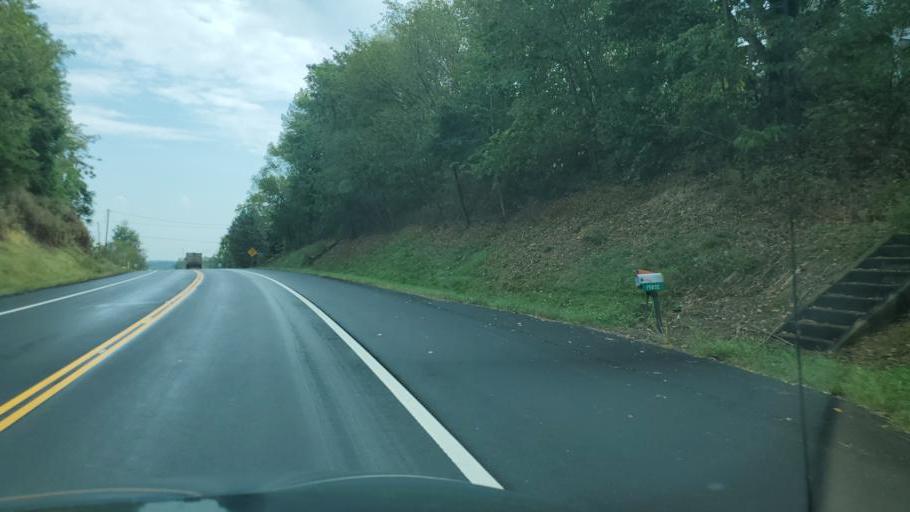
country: US
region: Ohio
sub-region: Perry County
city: Somerset
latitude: 39.9465
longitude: -82.2526
